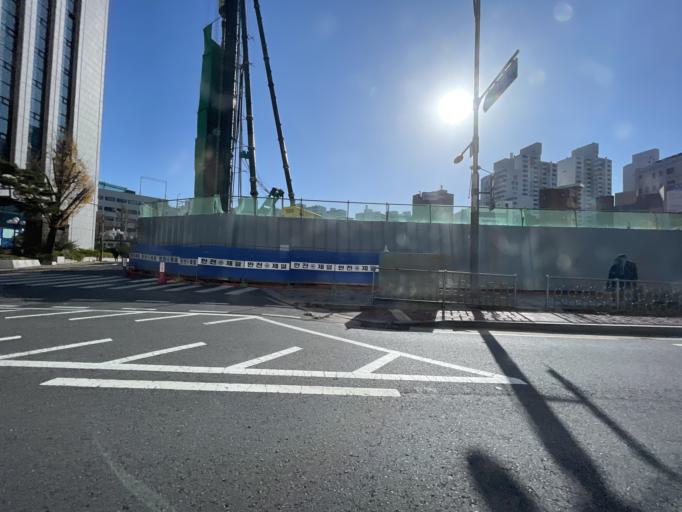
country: KR
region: Seoul
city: Seoul
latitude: 37.5391
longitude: 126.9456
